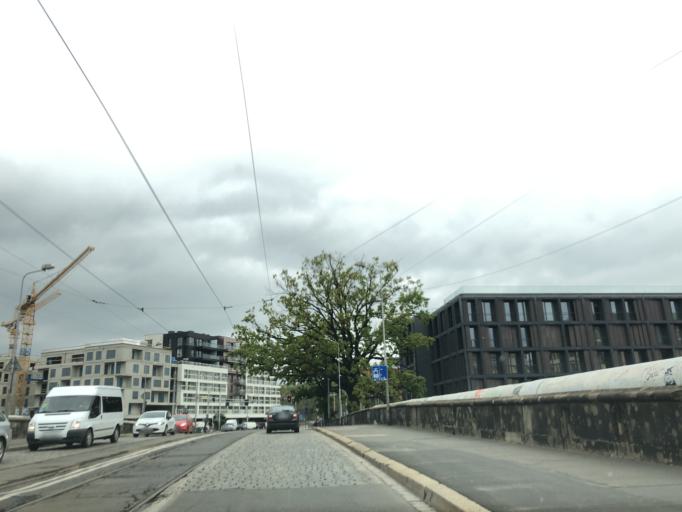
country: PL
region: Lower Silesian Voivodeship
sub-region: Powiat wroclawski
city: Wroclaw
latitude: 51.1135
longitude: 17.0315
